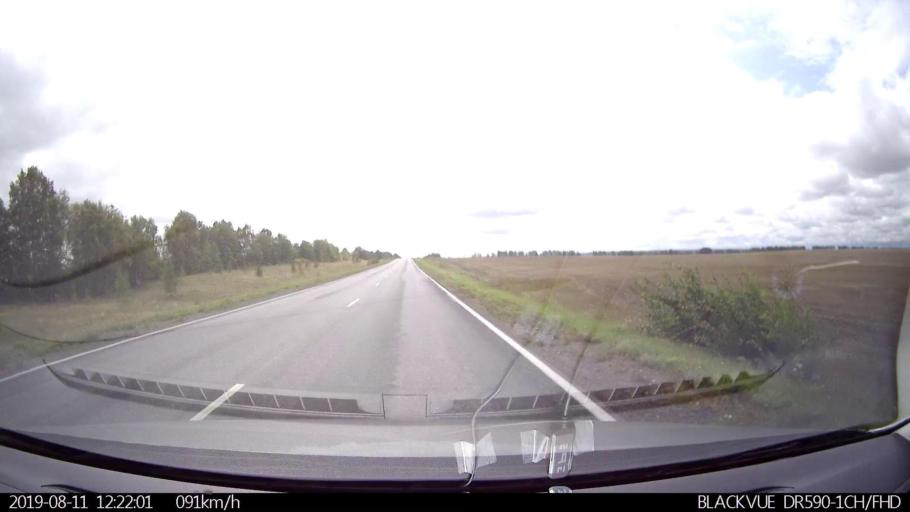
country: RU
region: Ulyanovsk
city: Ignatovka
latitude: 53.9145
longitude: 47.9560
